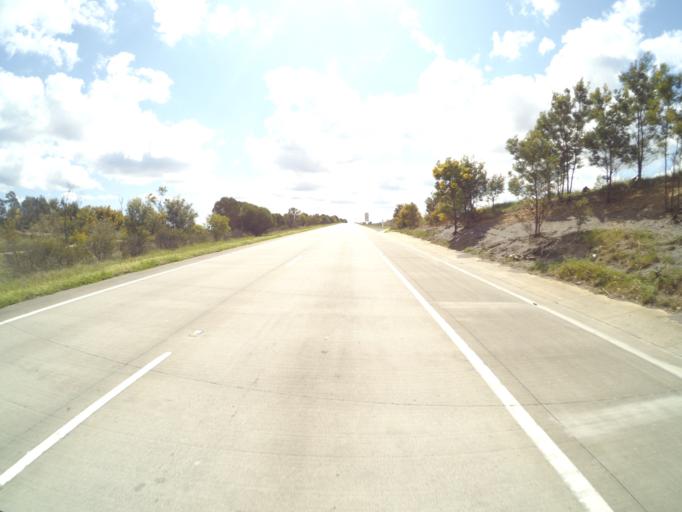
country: AU
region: New South Wales
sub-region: Wingecarribee
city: Moss Vale
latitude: -34.5035
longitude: 150.3101
